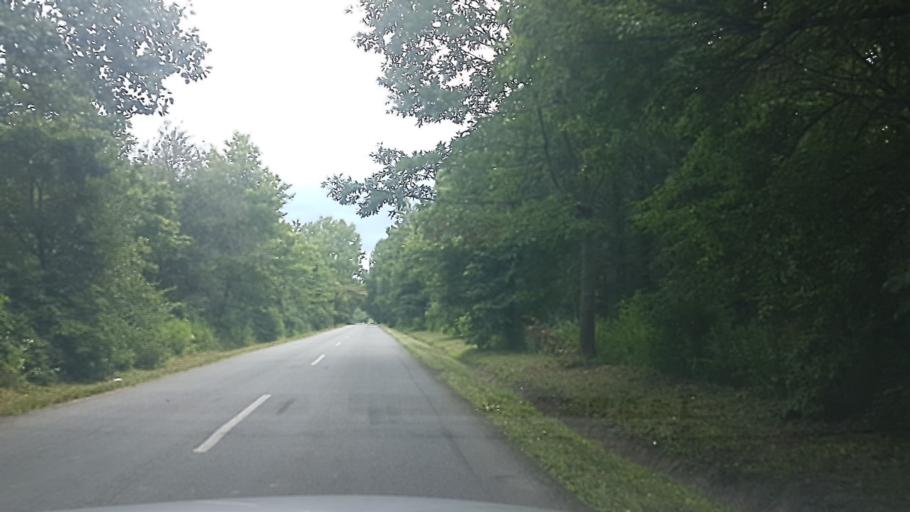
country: HU
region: Somogy
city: Barcs
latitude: 45.9431
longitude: 17.6345
